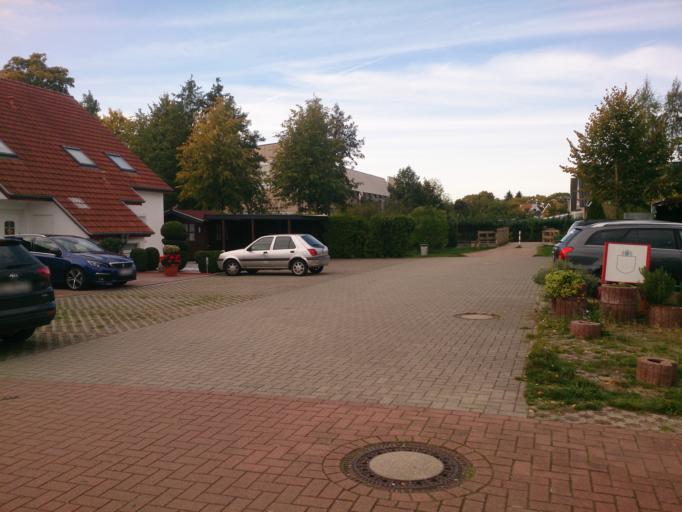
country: DE
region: Lower Saxony
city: Delmenhorst
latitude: 53.0614
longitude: 8.6347
